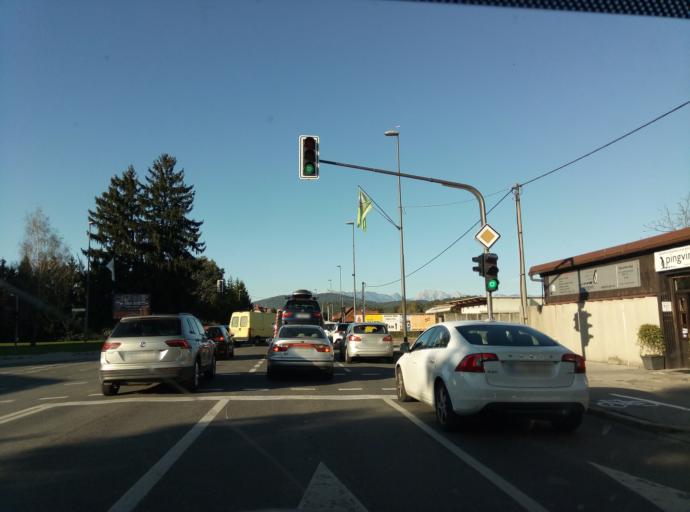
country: SI
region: Ljubljana
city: Ljubljana
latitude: 46.0892
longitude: 14.5141
